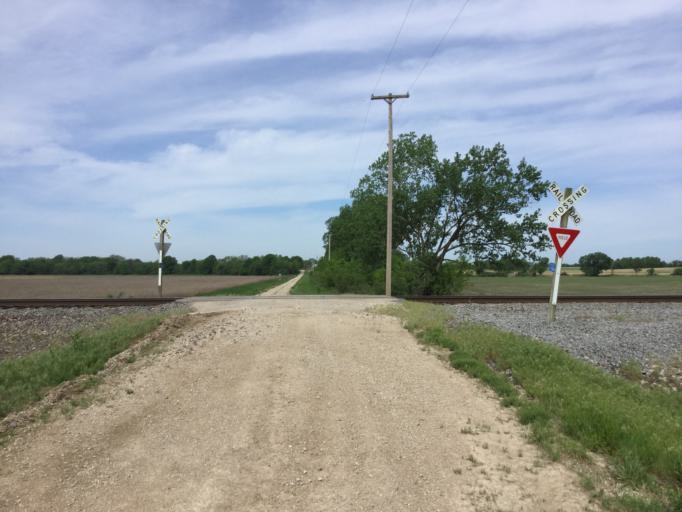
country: US
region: Kansas
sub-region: Coffey County
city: Burlington
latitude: 38.0461
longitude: -95.6373
